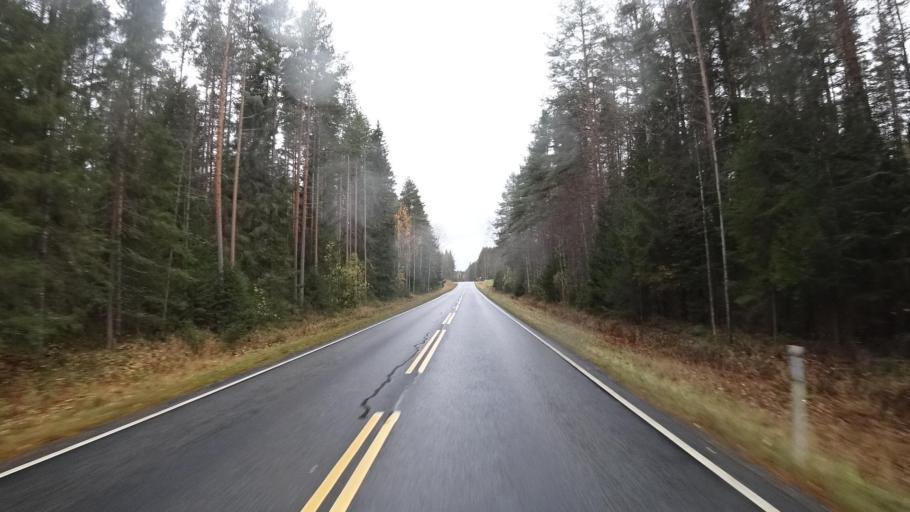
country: FI
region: Southern Savonia
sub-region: Mikkeli
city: Kangasniemi
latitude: 62.1624
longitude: 26.8358
